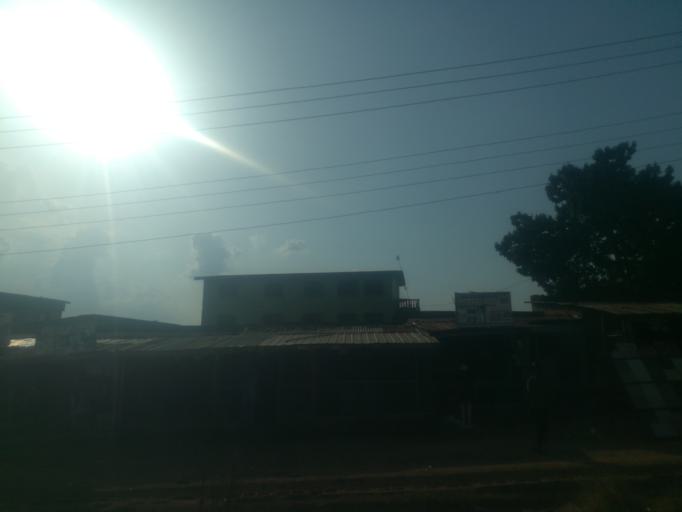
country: NG
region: Oyo
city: Moniya
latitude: 7.5114
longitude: 3.9127
